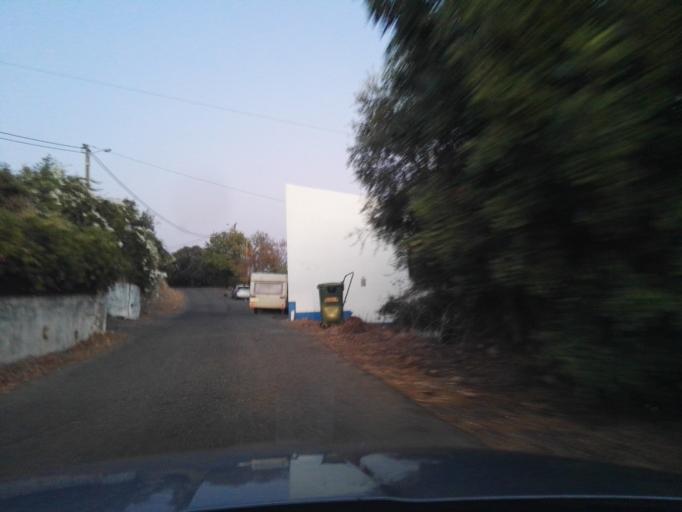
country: PT
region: Faro
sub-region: Sao Bras de Alportel
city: Sao Bras de Alportel
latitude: 37.1559
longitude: -7.9405
